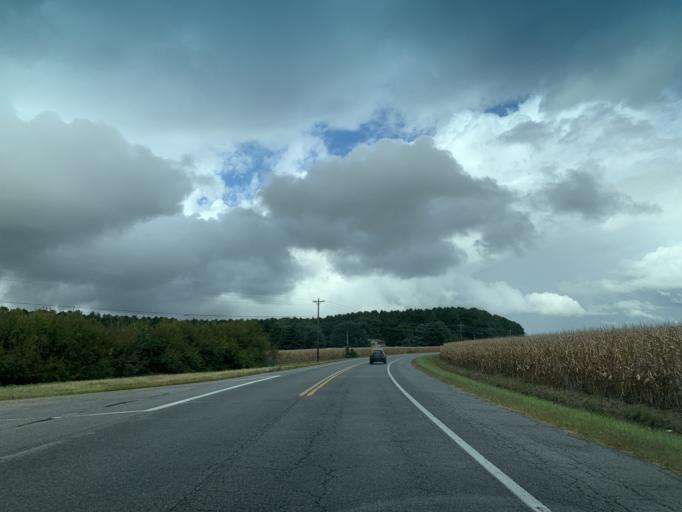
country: US
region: Maryland
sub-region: Caroline County
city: Greensboro
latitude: 39.1014
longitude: -75.8739
